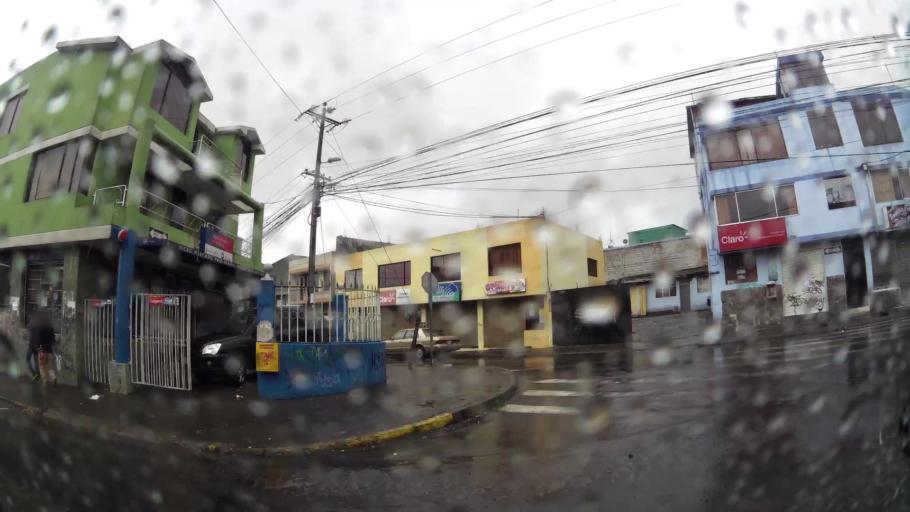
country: EC
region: Pichincha
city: Quito
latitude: -0.1070
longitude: -78.4972
